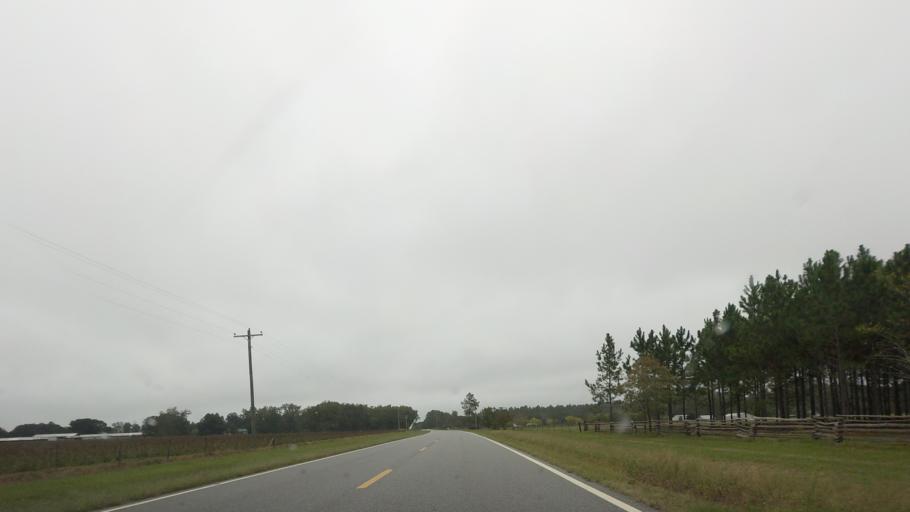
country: US
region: Georgia
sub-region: Berrien County
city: Enigma
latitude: 31.4491
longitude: -83.2391
